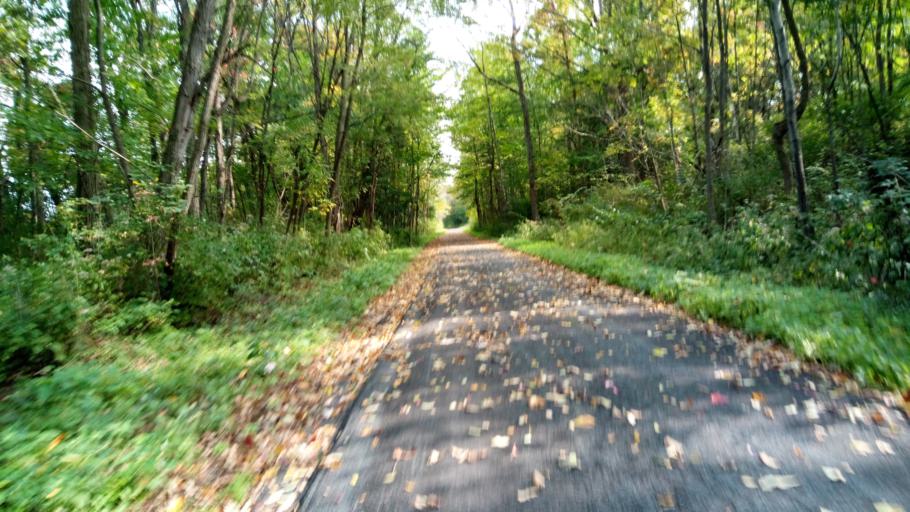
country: US
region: New York
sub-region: Wayne County
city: Clyde
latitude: 43.0672
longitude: -76.8516
